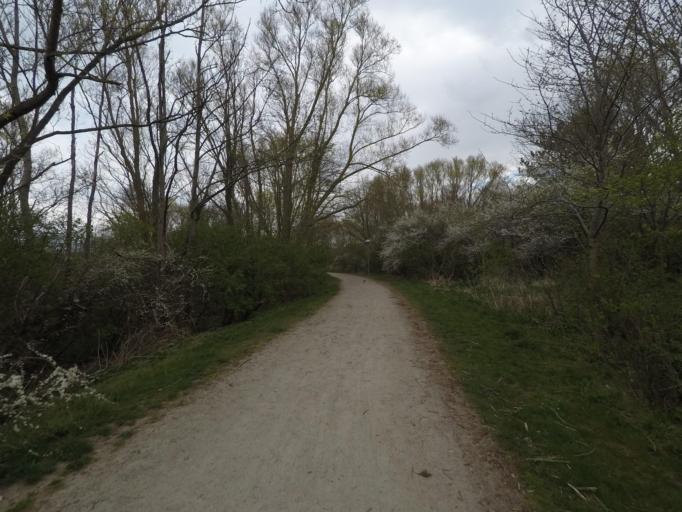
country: SE
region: Skane
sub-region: Lomma Kommun
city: Lomma
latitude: 55.6685
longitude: 13.0640
